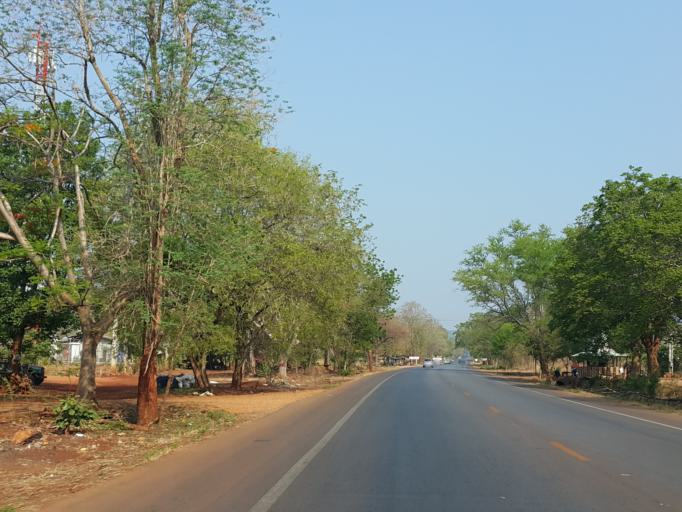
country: TH
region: Kanchanaburi
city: Sai Yok
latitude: 14.1001
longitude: 99.2316
